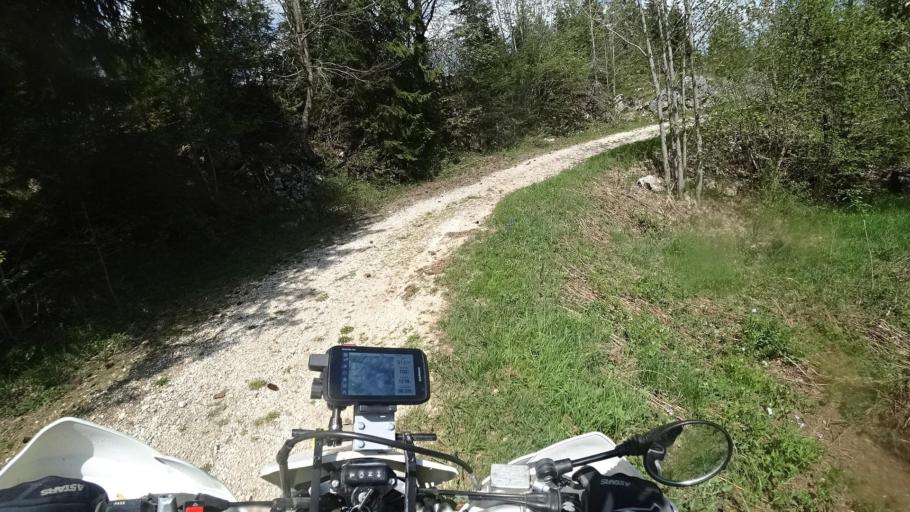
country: BA
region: Republika Srpska
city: Sipovo
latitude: 44.0665
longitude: 17.0955
